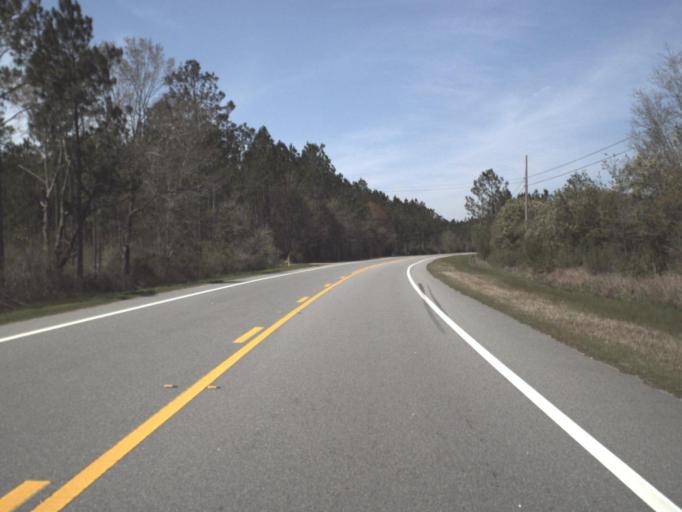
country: US
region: Florida
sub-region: Bay County
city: Lynn Haven
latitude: 30.3282
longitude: -85.7386
